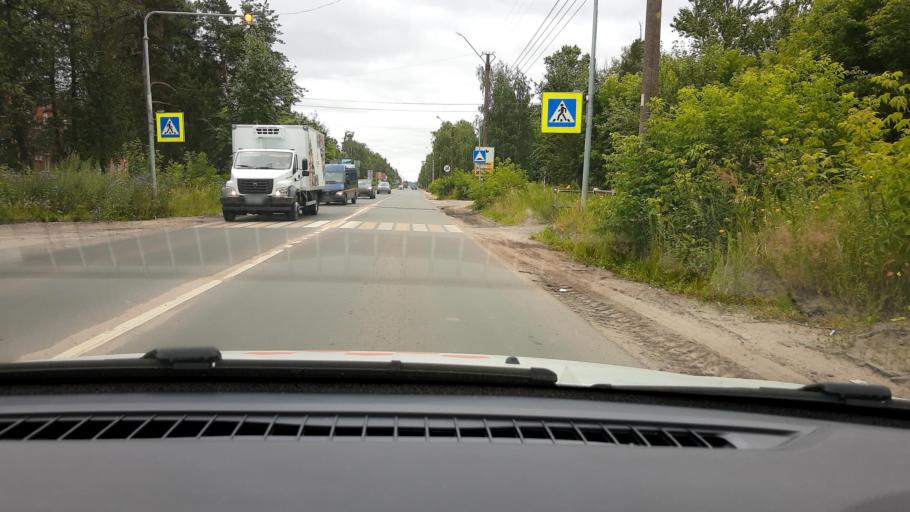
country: RU
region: Nizjnij Novgorod
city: Pyra
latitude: 56.2456
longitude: 43.3906
